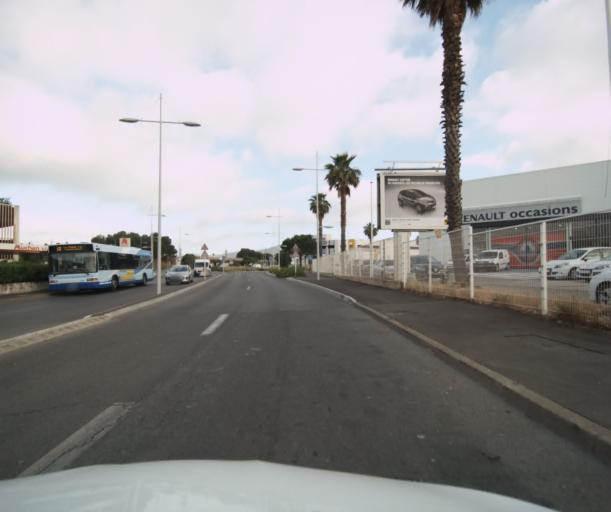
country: FR
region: Provence-Alpes-Cote d'Azur
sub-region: Departement du Var
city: Six-Fours-les-Plages
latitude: 43.1128
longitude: 5.8587
